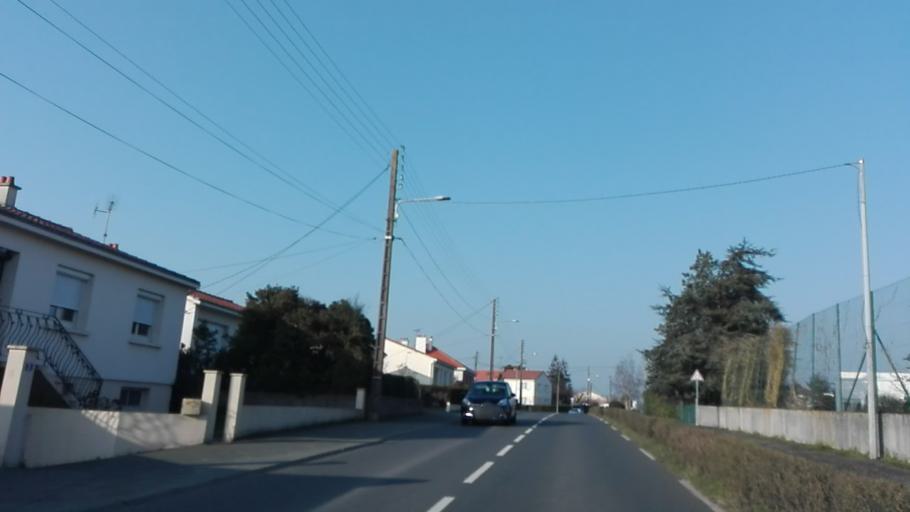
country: FR
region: Pays de la Loire
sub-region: Departement de la Vendee
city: Montaigu
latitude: 46.9693
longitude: -1.3080
